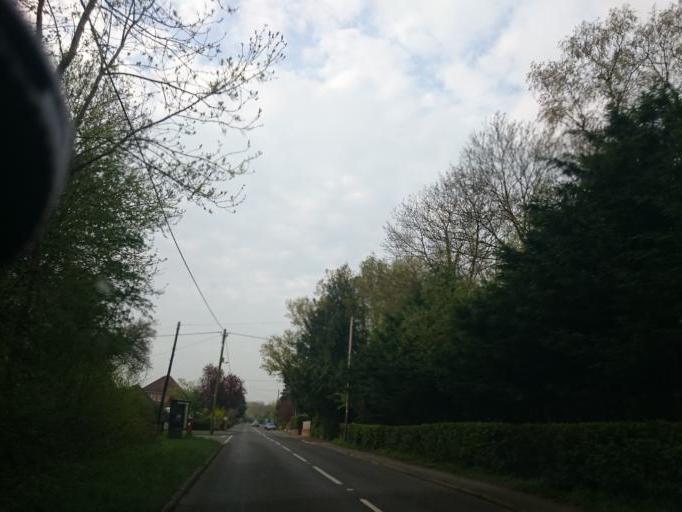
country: GB
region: England
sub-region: Surrey
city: Seale
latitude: 51.2399
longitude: -0.7091
